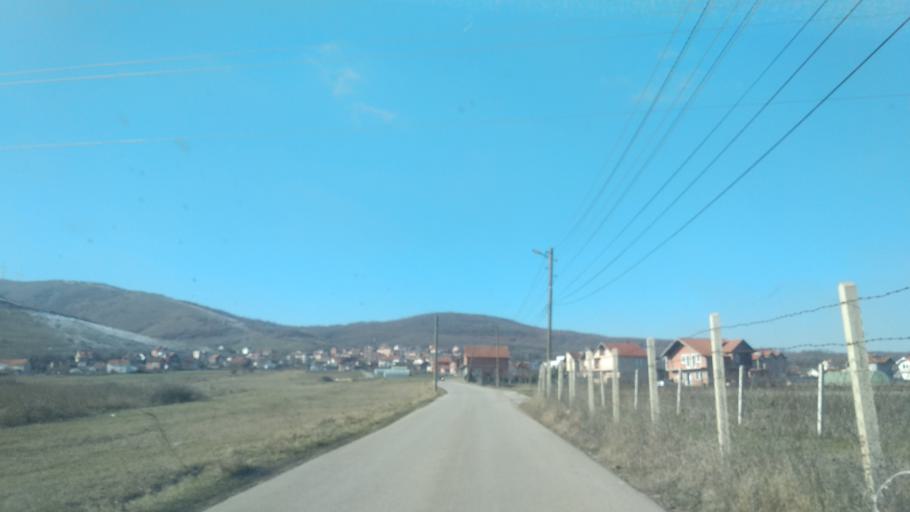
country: XK
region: Pristina
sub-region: Komuna e Gracanices
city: Glanica
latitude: 42.5833
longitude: 21.0100
